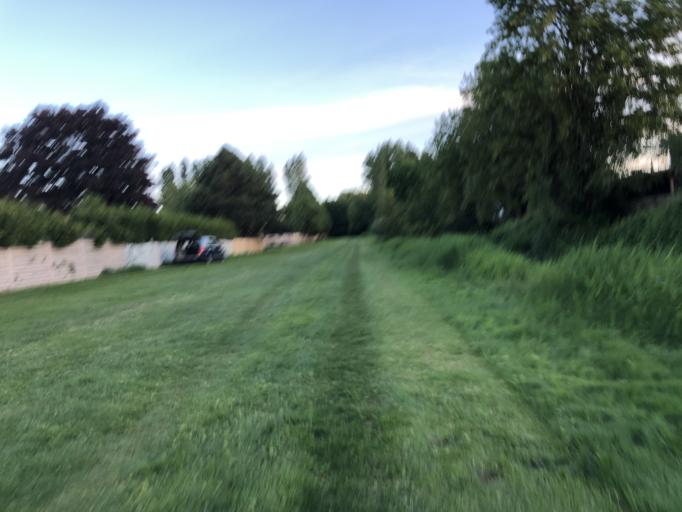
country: CA
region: British Columbia
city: Richmond
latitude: 49.1370
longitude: -123.1253
